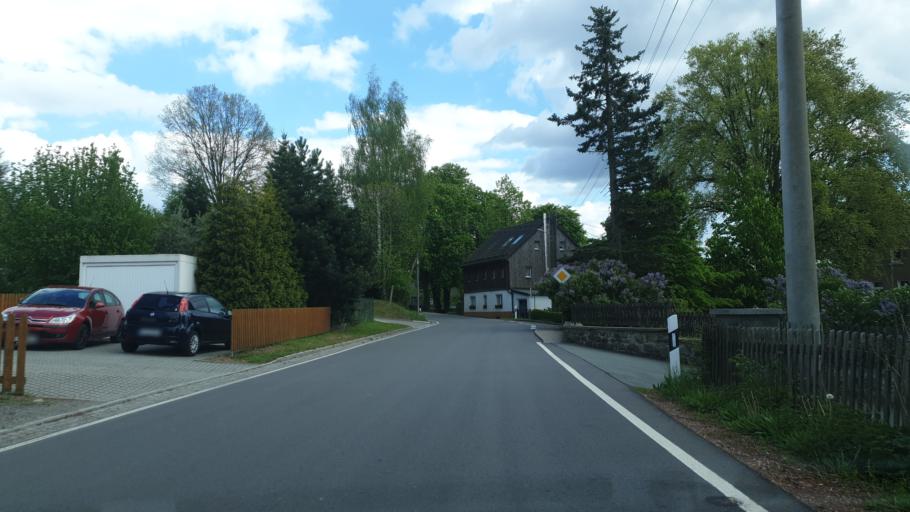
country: DE
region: Saxony
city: Kirchberg
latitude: 50.7805
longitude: 12.7744
